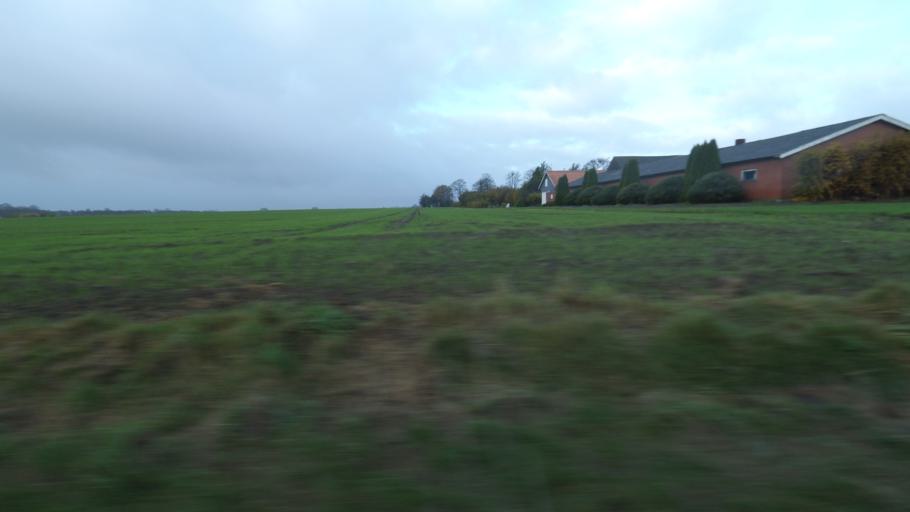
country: DK
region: Central Jutland
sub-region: Odder Kommune
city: Odder
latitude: 55.9519
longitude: 10.2369
